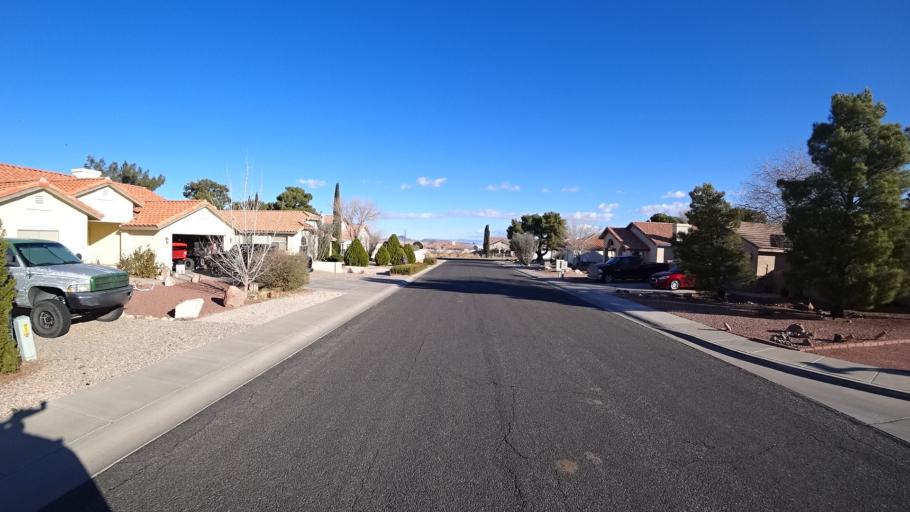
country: US
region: Arizona
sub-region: Mohave County
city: New Kingman-Butler
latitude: 35.2232
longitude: -113.9755
